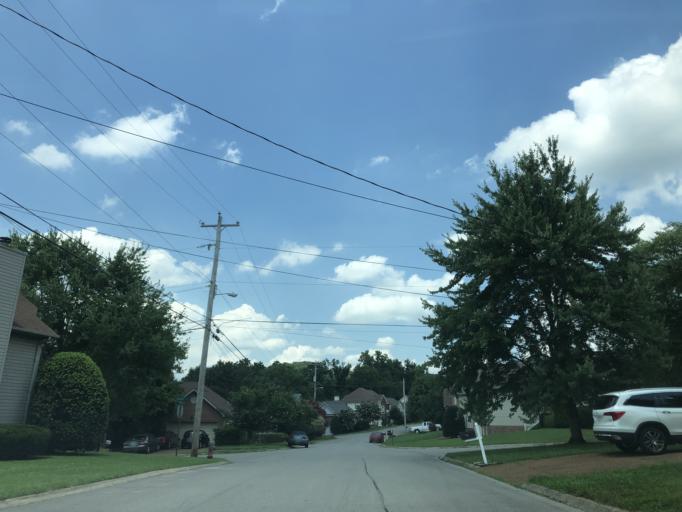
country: US
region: Tennessee
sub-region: Williamson County
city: Brentwood Estates
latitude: 36.0210
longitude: -86.7221
